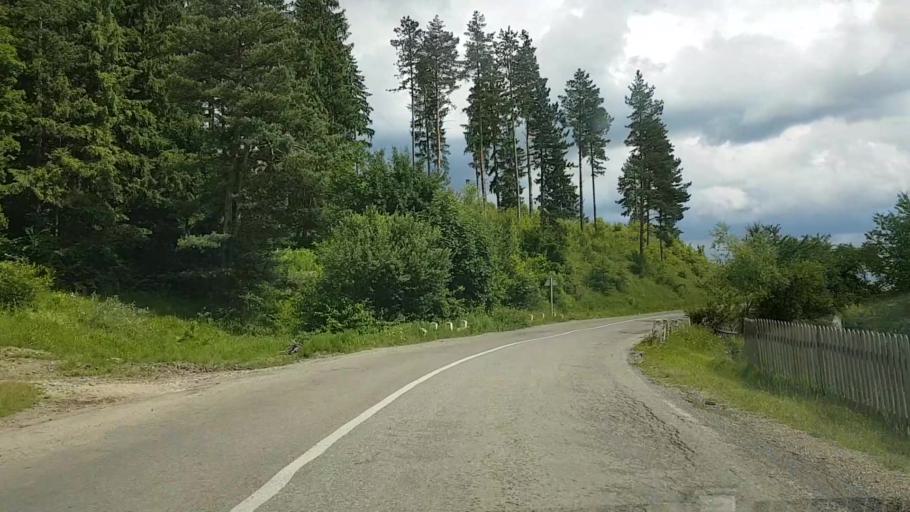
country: RO
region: Neamt
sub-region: Comuna Hangu
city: Hangu
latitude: 47.0089
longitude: 26.0896
